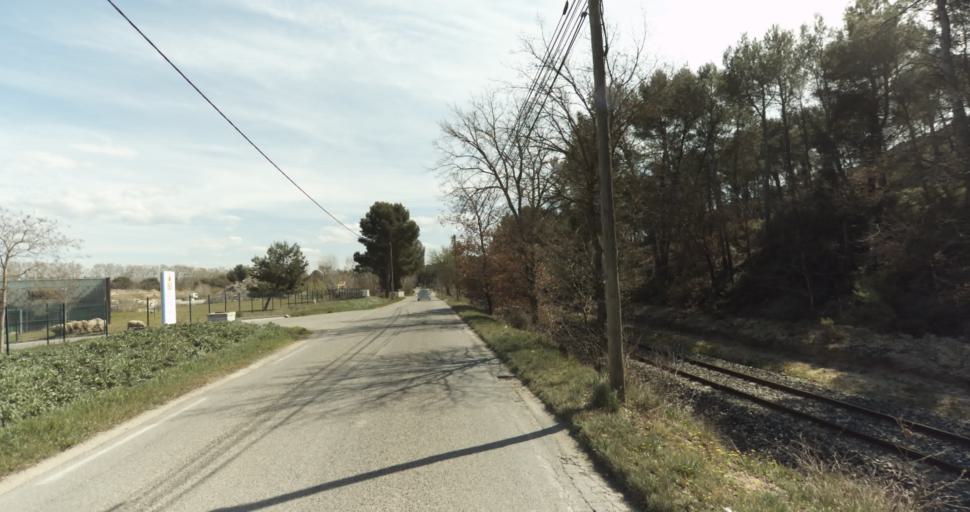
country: FR
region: Provence-Alpes-Cote d'Azur
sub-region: Departement des Bouches-du-Rhone
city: Ventabren
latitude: 43.5060
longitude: 5.3350
